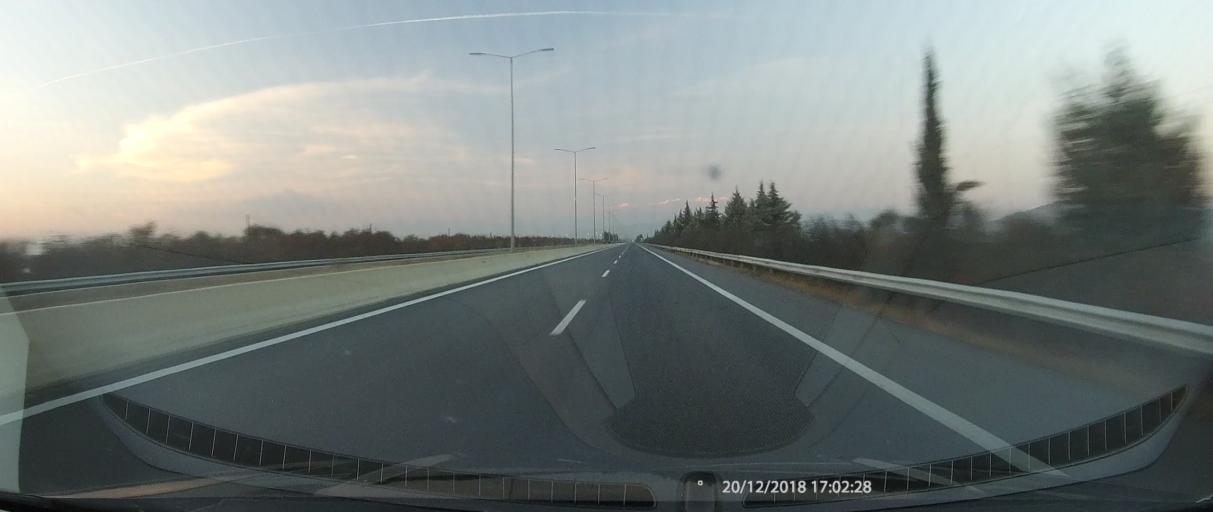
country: GR
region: Thessaly
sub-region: Nomos Larisis
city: Platykampos
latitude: 39.6767
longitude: 22.4976
